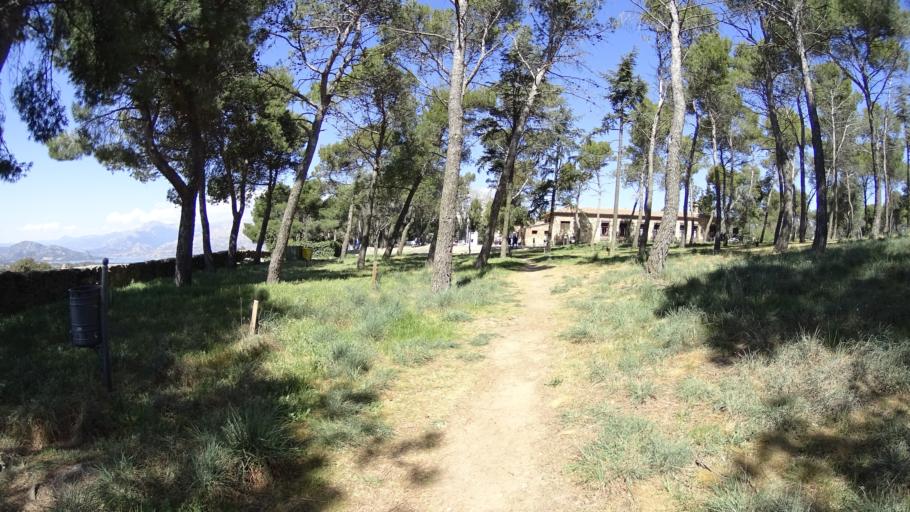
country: ES
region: Madrid
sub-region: Provincia de Madrid
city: Colmenar Viejo
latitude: 40.7021
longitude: -3.7696
